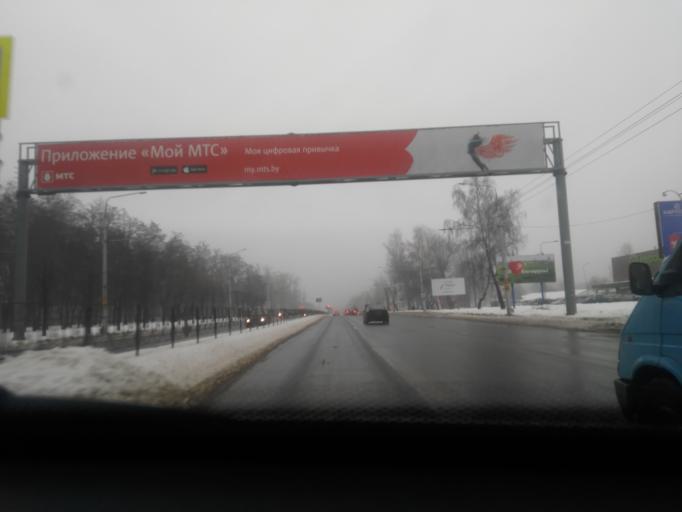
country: BY
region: Mogilev
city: Babruysk
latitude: 53.1667
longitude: 29.2079
